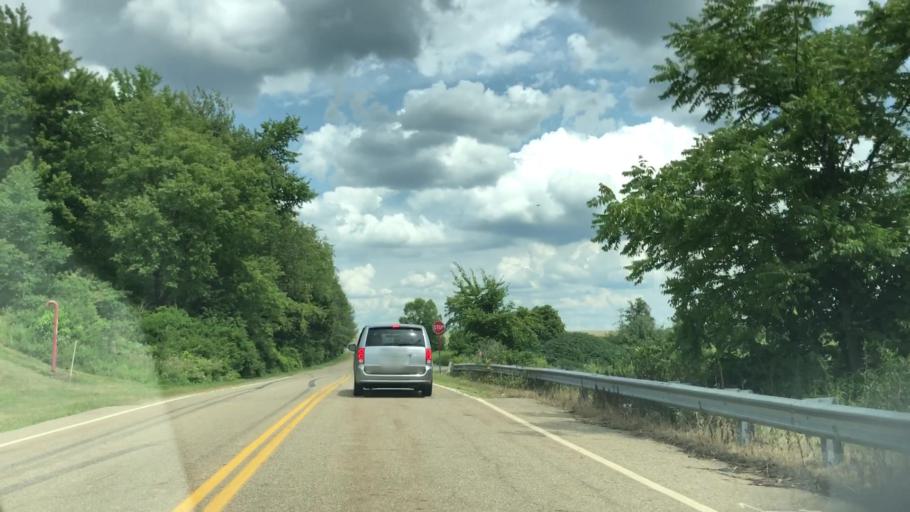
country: US
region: Ohio
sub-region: Summit County
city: Greensburg
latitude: 40.9074
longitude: -81.4469
